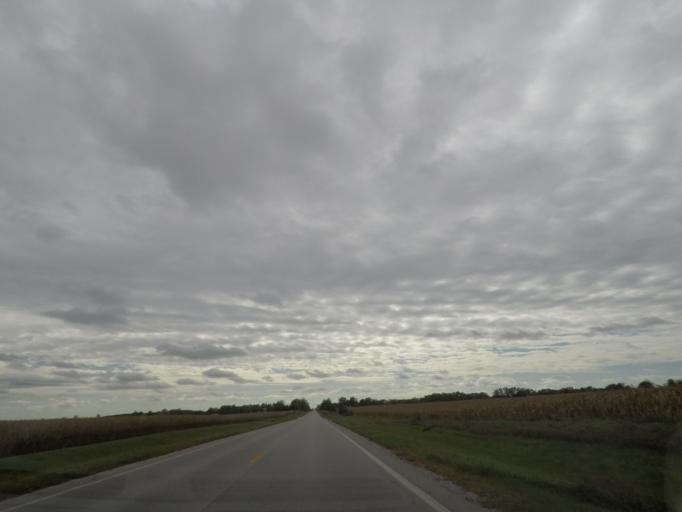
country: US
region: Iowa
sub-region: Story County
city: Huxley
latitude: 41.8759
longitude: -93.5314
